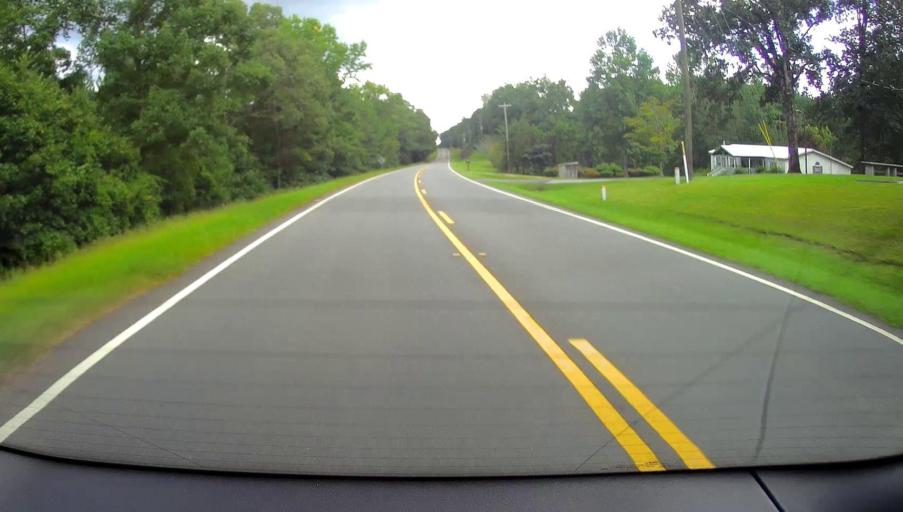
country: US
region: Georgia
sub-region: Monroe County
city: Forsyth
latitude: 32.8841
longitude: -83.9388
